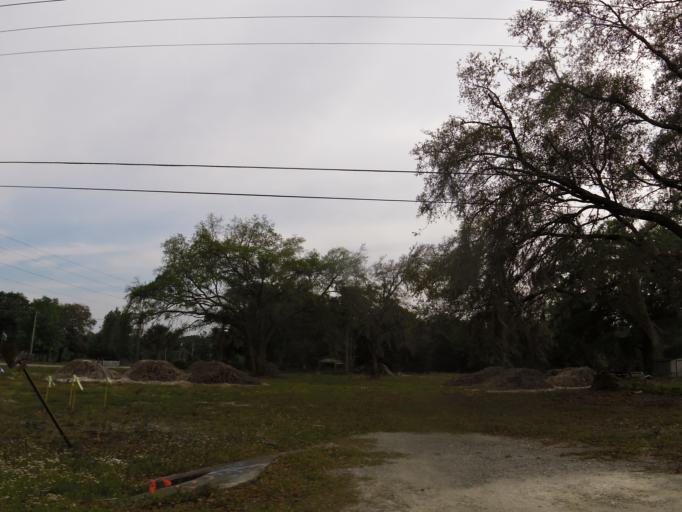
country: US
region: Florida
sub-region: Nassau County
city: Hilliard
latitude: 30.6976
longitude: -81.9063
